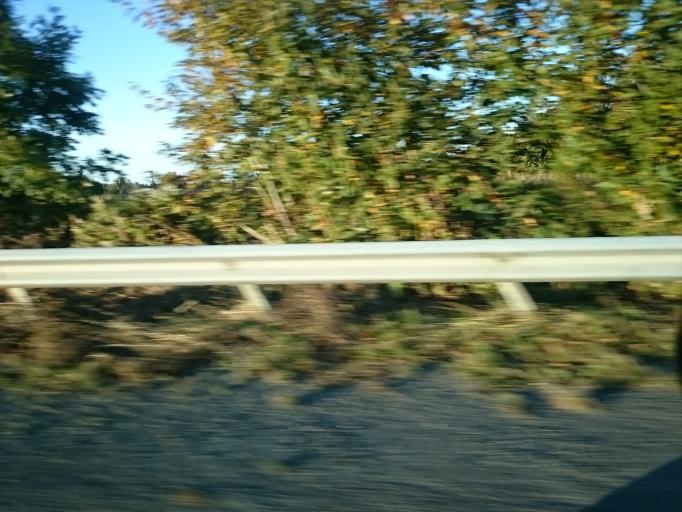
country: FR
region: Brittany
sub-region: Departement des Cotes-d'Armor
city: Graces
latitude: 48.5667
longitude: -3.2259
